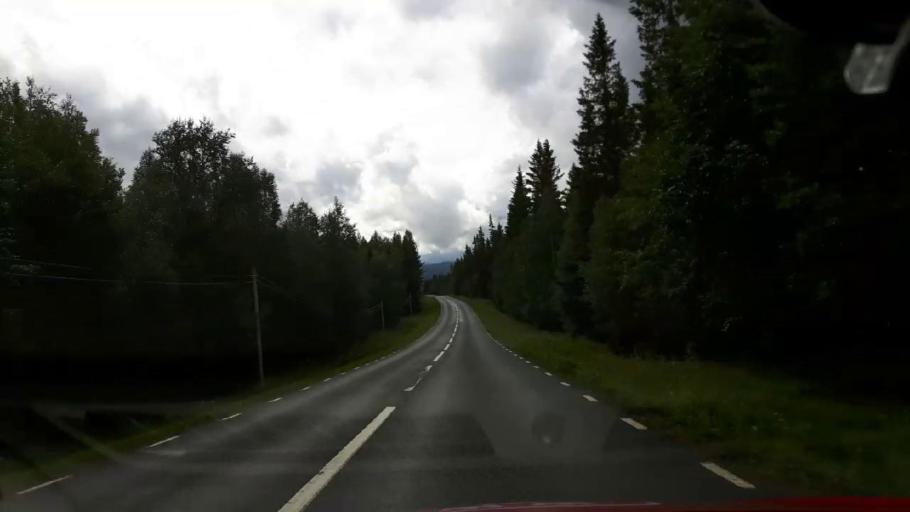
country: NO
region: Nord-Trondelag
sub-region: Lierne
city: Sandvika
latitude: 64.5171
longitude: 14.1604
